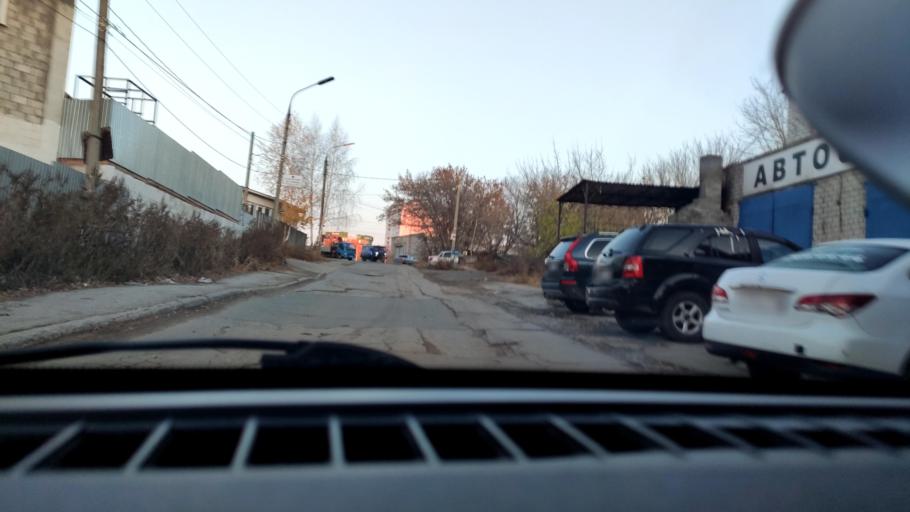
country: RU
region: Samara
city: Samara
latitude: 53.1813
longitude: 50.1112
